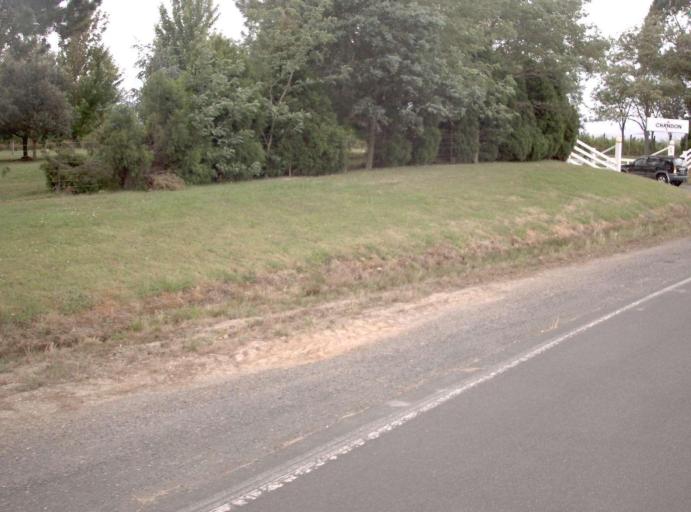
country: AU
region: Victoria
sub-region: Yarra Ranges
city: Yarra Glen
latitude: -37.6834
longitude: 145.4312
